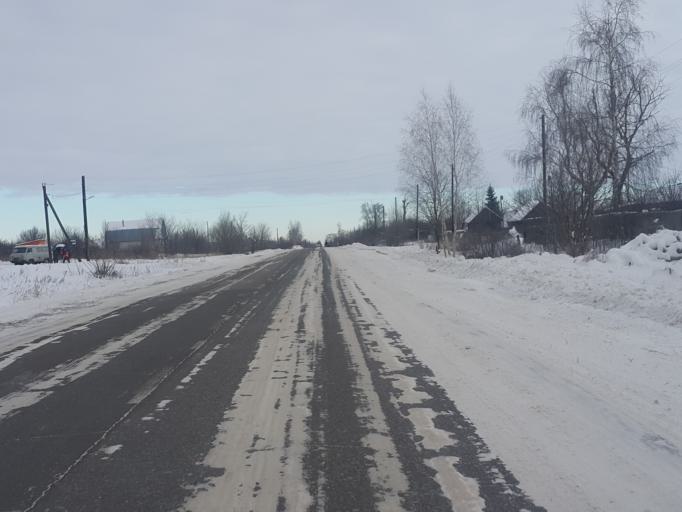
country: RU
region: Tambov
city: Platonovka
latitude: 52.8602
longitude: 41.8394
